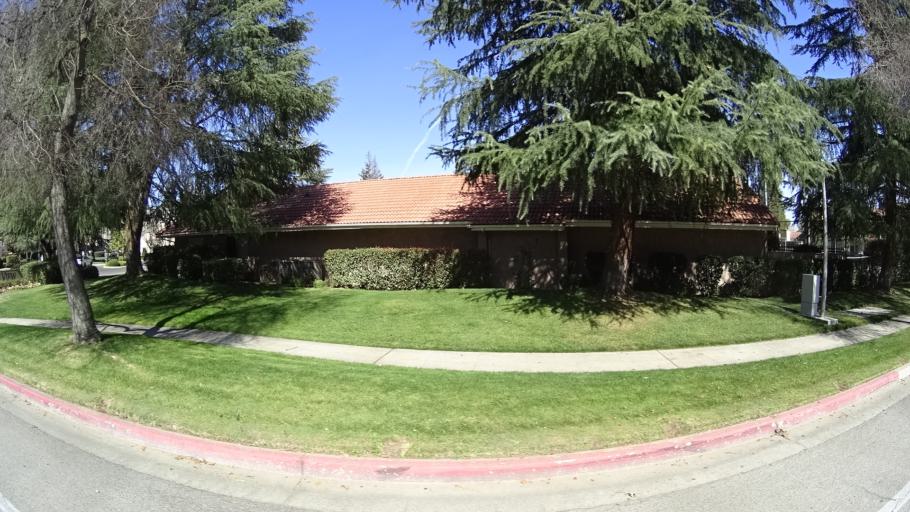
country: US
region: California
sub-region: Fresno County
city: Clovis
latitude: 36.8519
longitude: -119.7983
